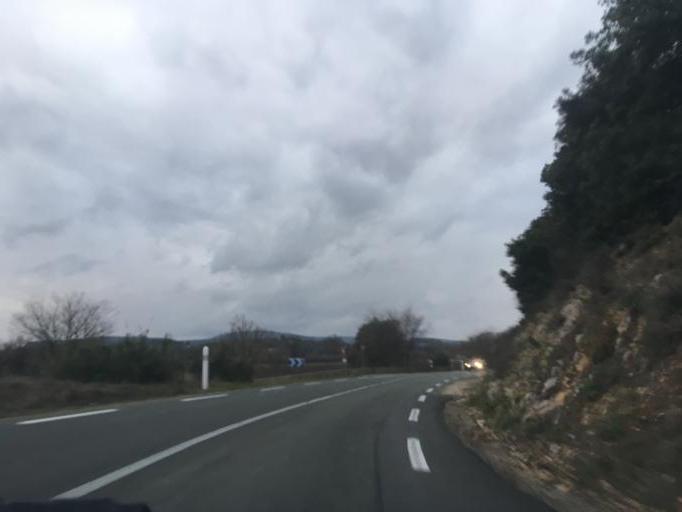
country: FR
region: Provence-Alpes-Cote d'Azur
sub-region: Departement du Var
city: Besse-sur-Issole
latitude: 43.3591
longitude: 6.1990
